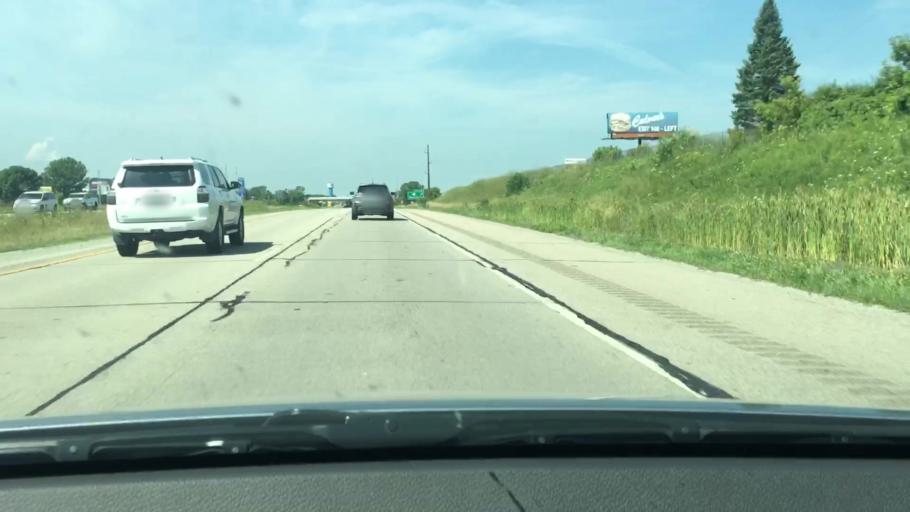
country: US
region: Wisconsin
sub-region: Outagamie County
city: Kaukauna
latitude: 44.3080
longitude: -88.2406
